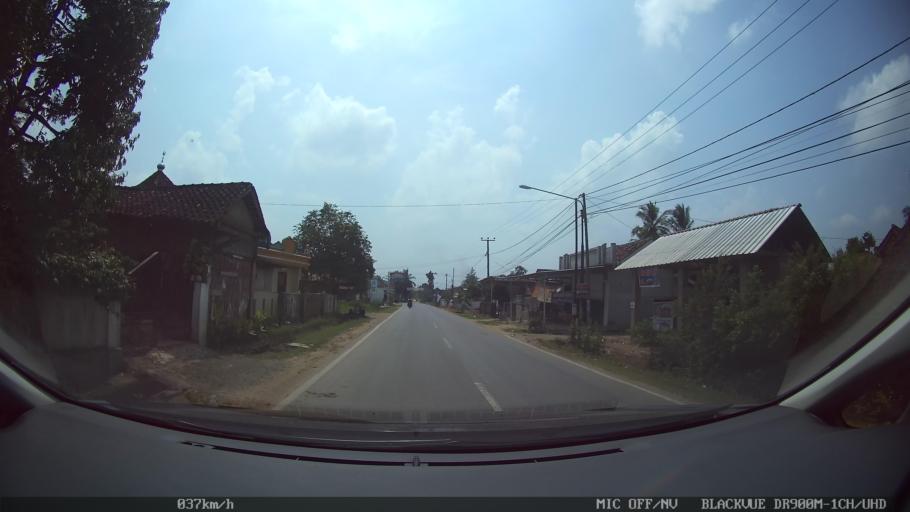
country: ID
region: Lampung
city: Pringsewu
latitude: -5.3875
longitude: 104.9680
